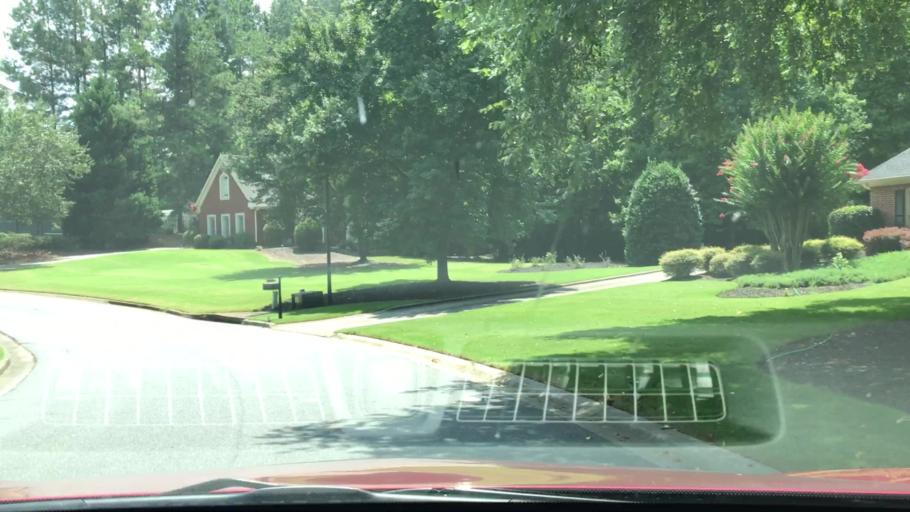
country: US
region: Georgia
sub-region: Forsyth County
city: Cumming
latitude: 34.1697
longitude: -84.1216
